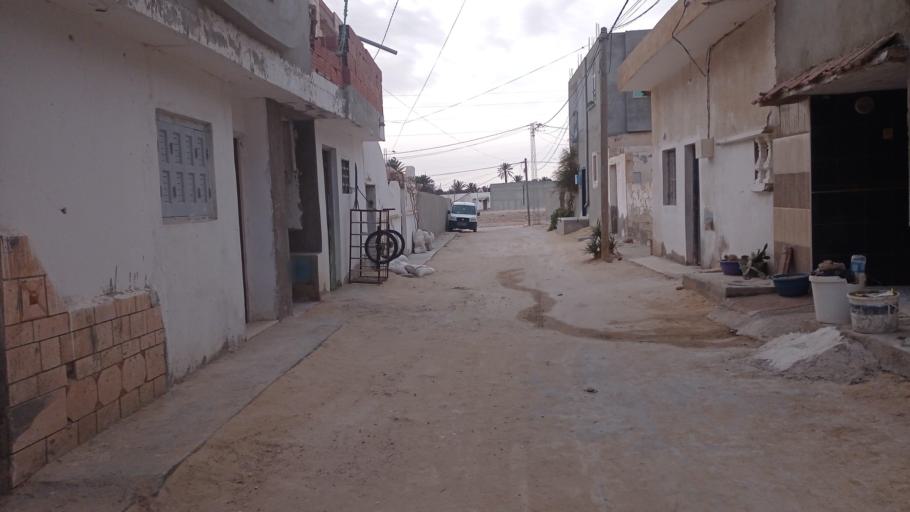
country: TN
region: Qabis
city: Gabes
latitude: 33.8362
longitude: 10.1154
